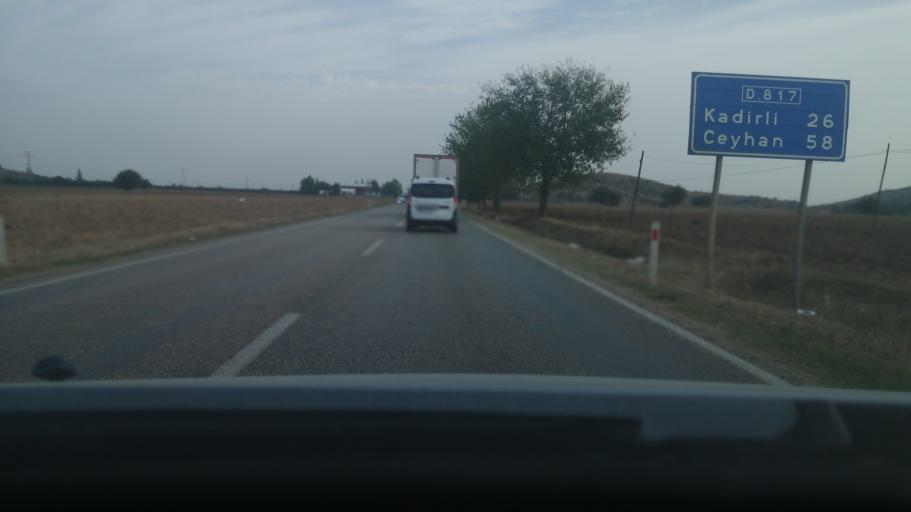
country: TR
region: Adana
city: Kozan
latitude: 37.3730
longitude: 35.8403
